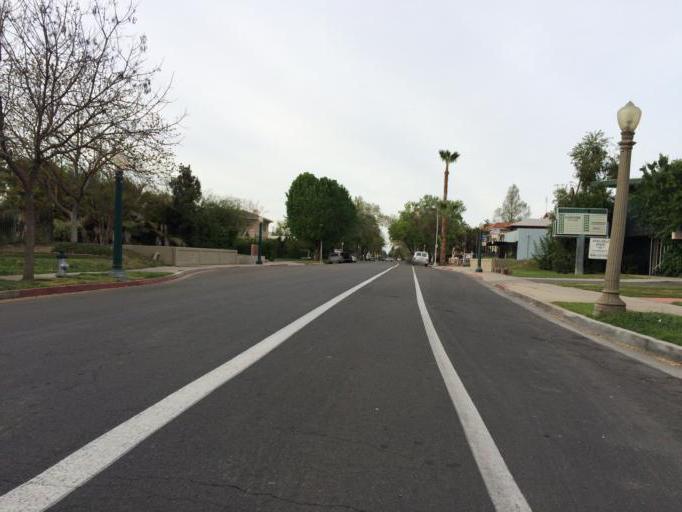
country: US
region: California
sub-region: Fresno County
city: Fresno
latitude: 36.7540
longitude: -119.7989
